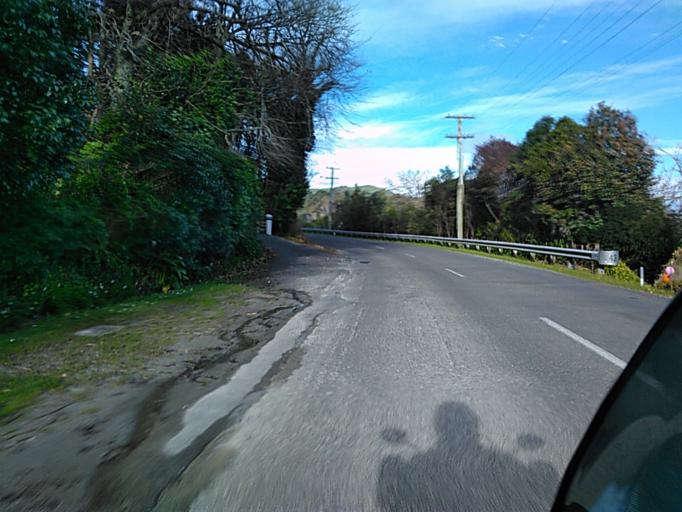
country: NZ
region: Gisborne
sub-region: Gisborne District
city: Gisborne
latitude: -38.6637
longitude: 178.0445
